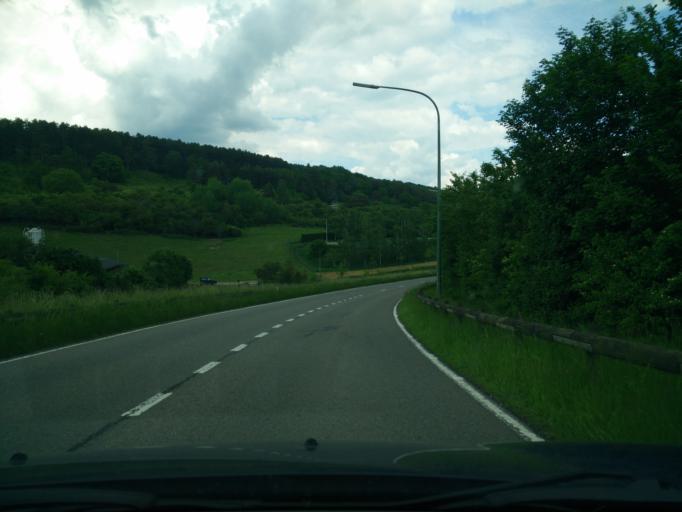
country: FR
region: Champagne-Ardenne
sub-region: Departement des Ardennes
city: Vireux-Molhain
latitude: 50.0822
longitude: 4.6274
